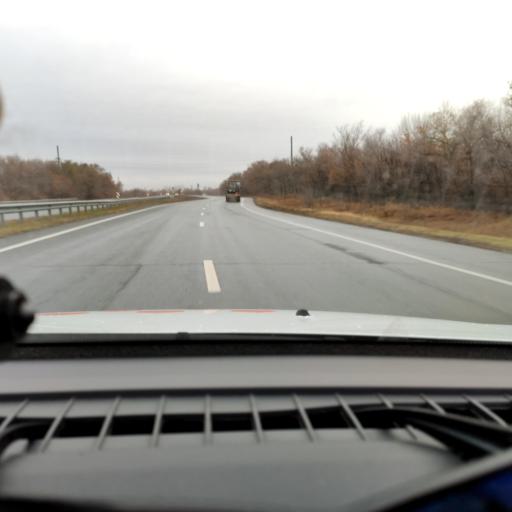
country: RU
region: Samara
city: Novokuybyshevsk
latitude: 53.0460
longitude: 50.0063
